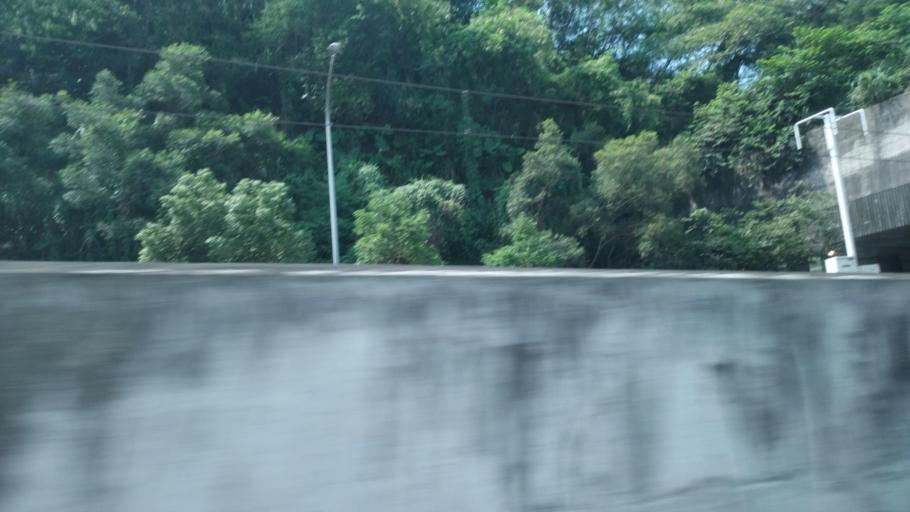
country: TW
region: Taipei
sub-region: Taipei
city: Banqiao
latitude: 24.9568
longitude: 121.5120
